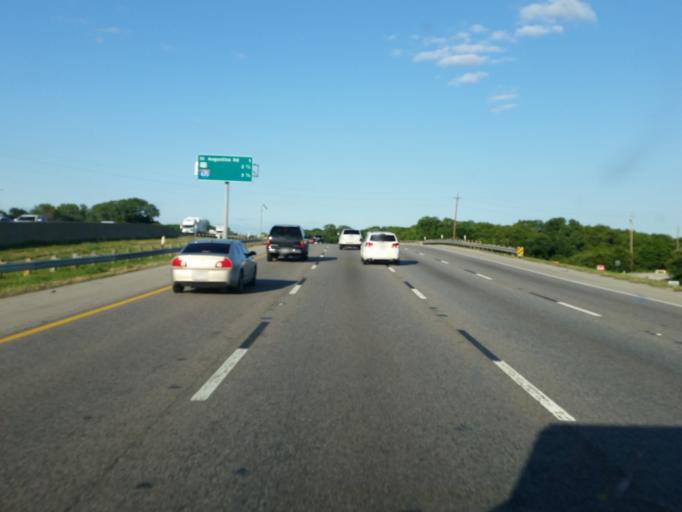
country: US
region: Texas
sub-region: Dallas County
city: Hutchins
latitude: 32.6786
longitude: -96.6774
